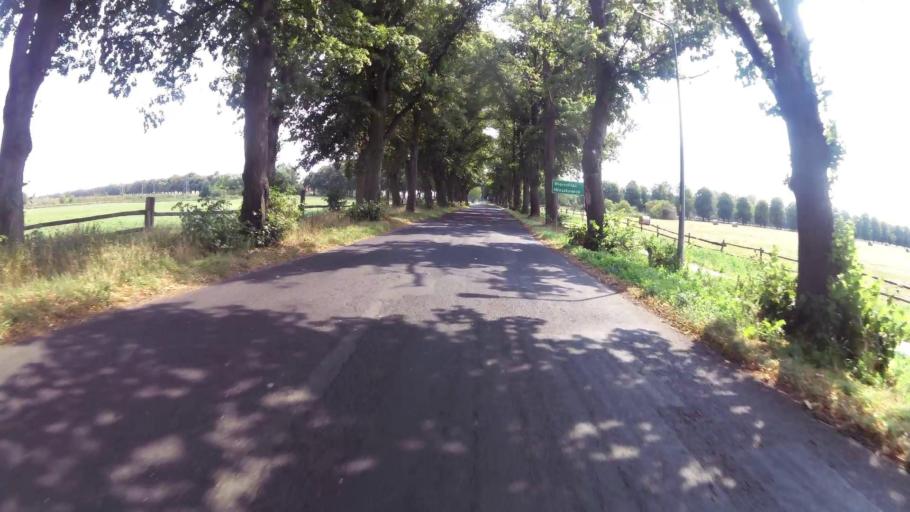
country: PL
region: West Pomeranian Voivodeship
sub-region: Powiat gryfinski
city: Mieszkowice
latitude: 52.8253
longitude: 14.4624
